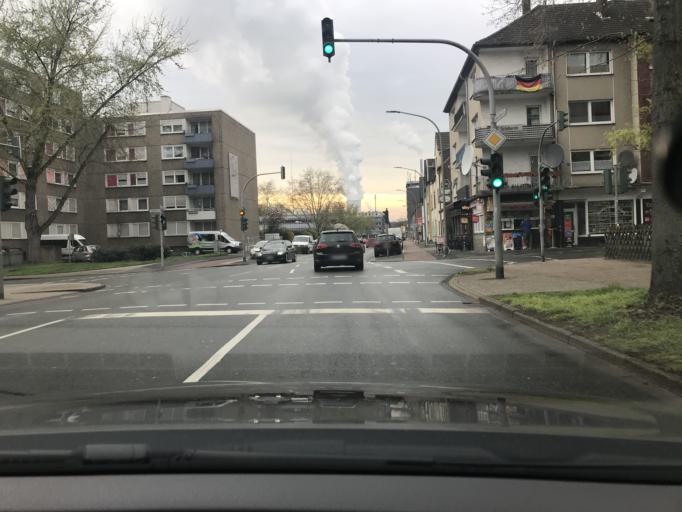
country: DE
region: North Rhine-Westphalia
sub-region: Regierungsbezirk Dusseldorf
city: Dinslaken
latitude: 51.5273
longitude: 6.7471
